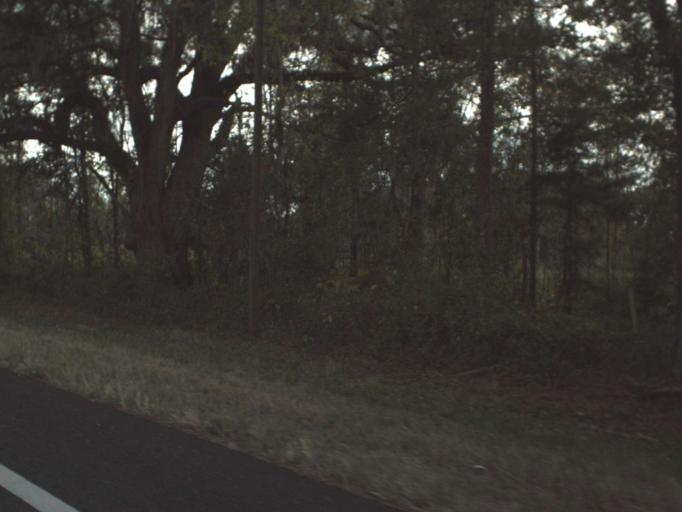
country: US
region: Florida
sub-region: Gadsden County
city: Havana
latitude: 30.5973
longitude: -84.4154
